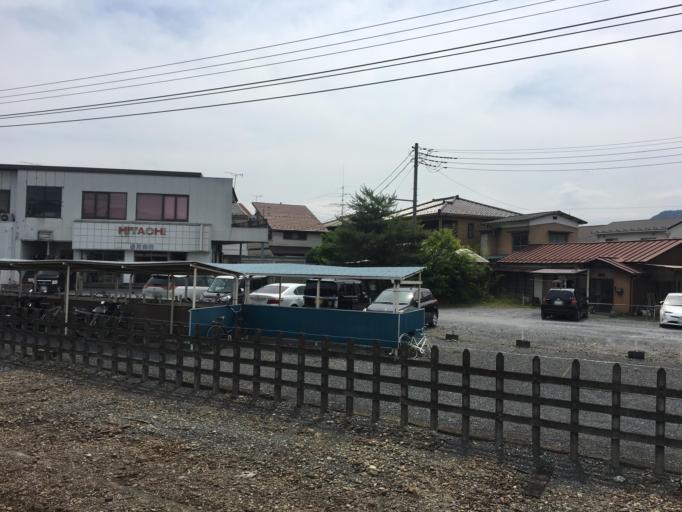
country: JP
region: Saitama
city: Chichibu
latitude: 36.0685
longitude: 139.0940
